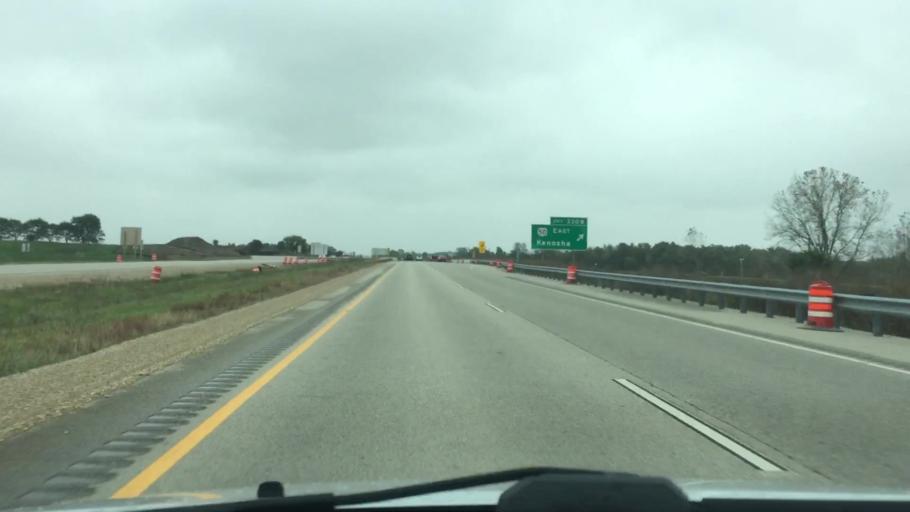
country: US
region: Wisconsin
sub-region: Walworth County
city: Lake Geneva
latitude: 42.5959
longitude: -88.4104
